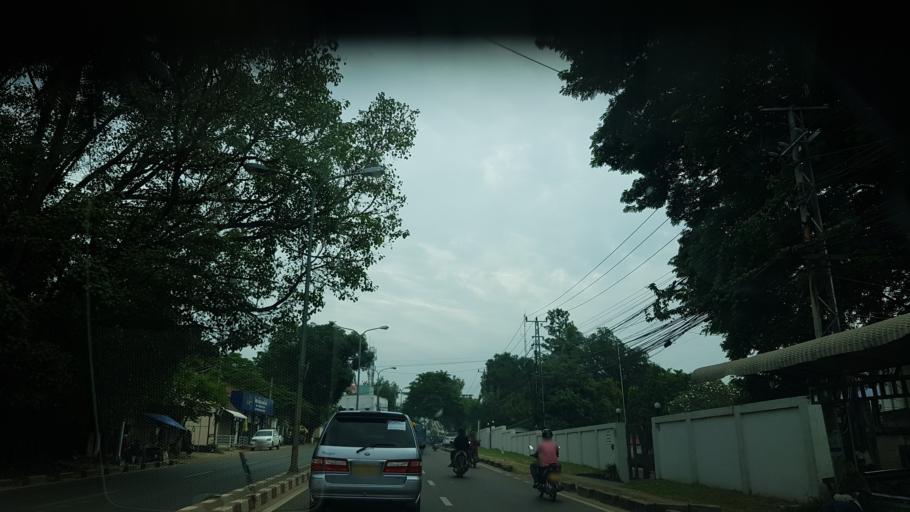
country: LA
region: Vientiane
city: Vientiane
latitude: 17.9389
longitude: 102.6179
